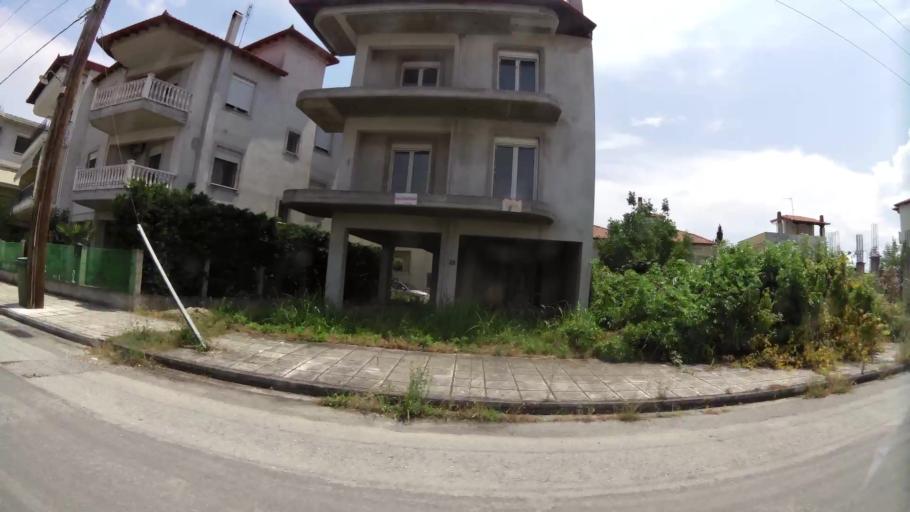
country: GR
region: Central Macedonia
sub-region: Nomos Pierias
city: Peristasi
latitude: 40.2732
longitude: 22.5340
